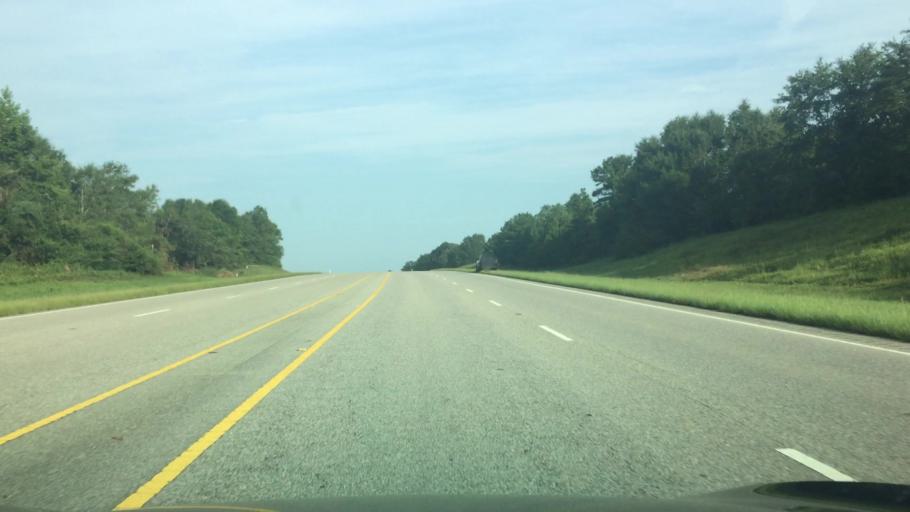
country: US
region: Alabama
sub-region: Butler County
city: Georgiana
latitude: 31.4603
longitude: -86.6421
